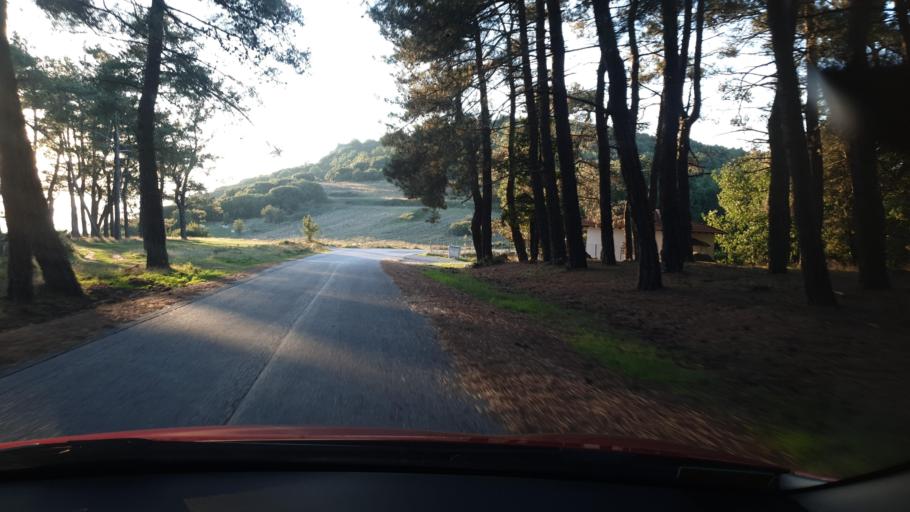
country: GR
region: Central Macedonia
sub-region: Nomos Thessalonikis
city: Peristera
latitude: 40.5130
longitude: 23.2155
